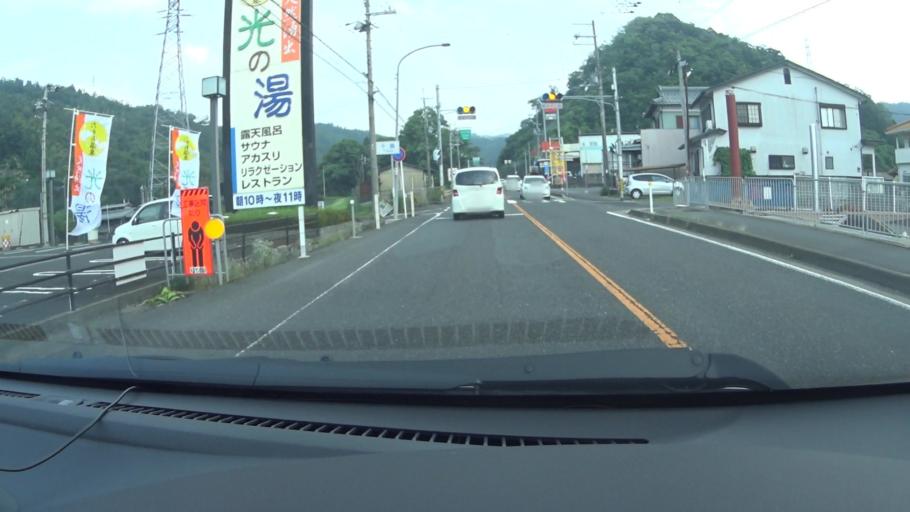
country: JP
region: Kyoto
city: Maizuru
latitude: 35.4210
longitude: 135.3300
